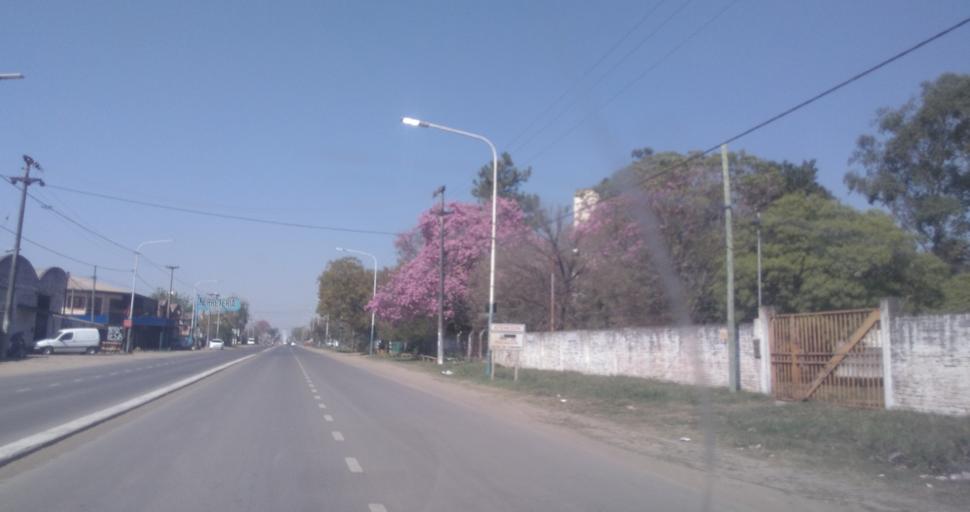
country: AR
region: Chaco
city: Fontana
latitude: -27.4280
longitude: -59.0270
